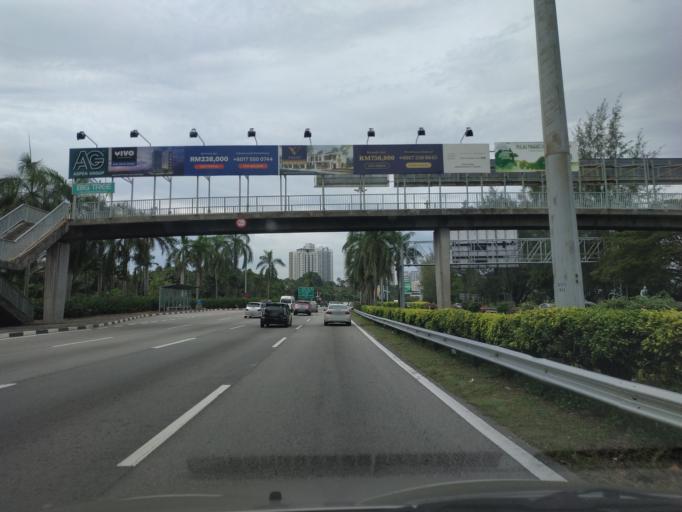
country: MY
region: Penang
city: George Town
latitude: 5.3684
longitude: 100.3140
